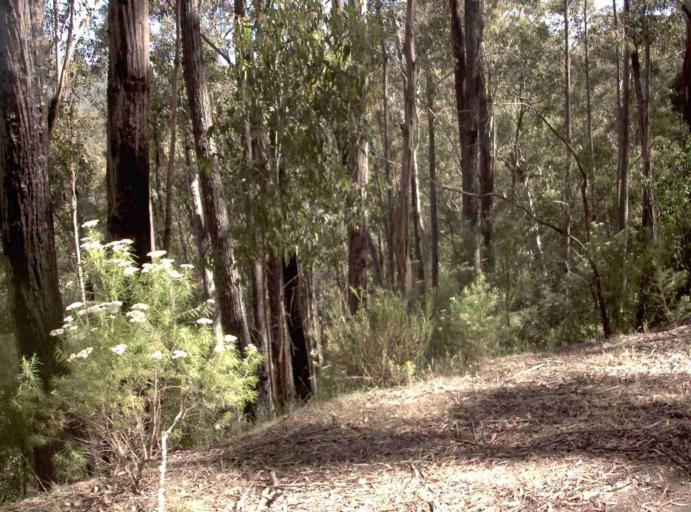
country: AU
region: Victoria
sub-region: East Gippsland
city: Lakes Entrance
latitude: -37.3944
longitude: 148.1225
